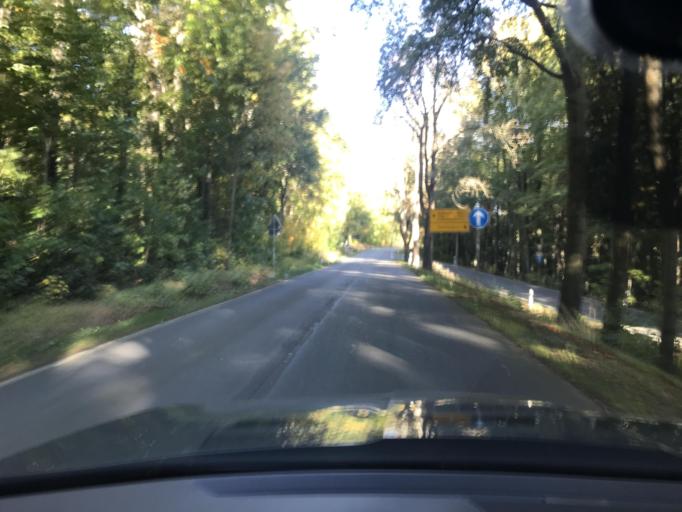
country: DE
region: Saxony-Anhalt
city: Friedrichsbrunn
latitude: 51.6836
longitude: 11.0195
